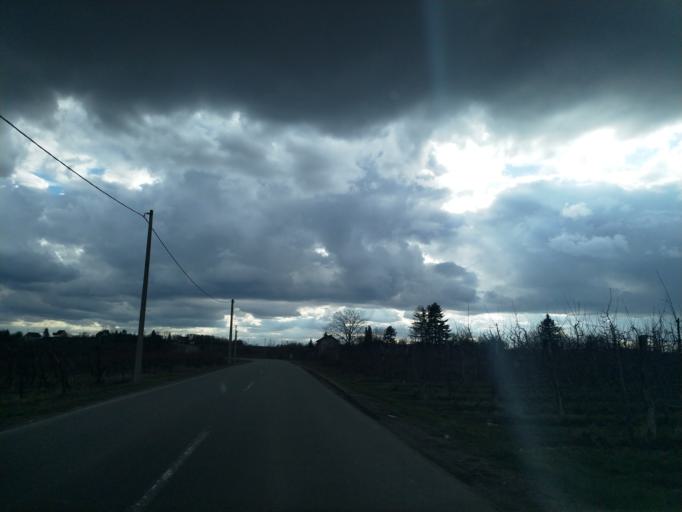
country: RS
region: Central Serbia
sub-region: Belgrade
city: Grocka
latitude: 44.6268
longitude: 20.7437
